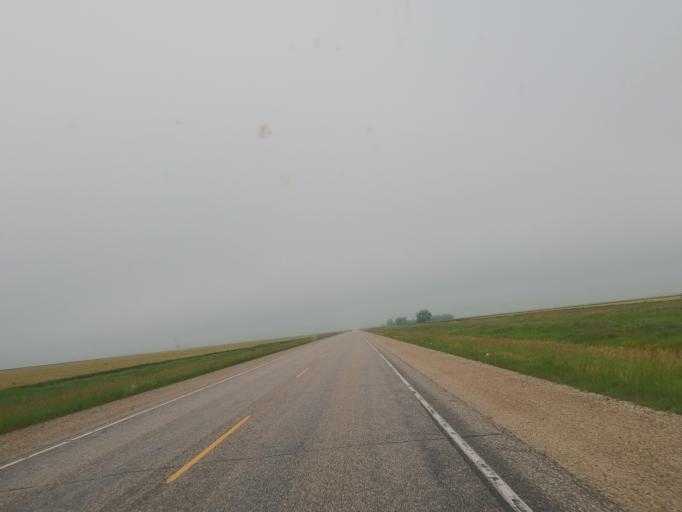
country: CA
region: Manitoba
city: Carman
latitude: 49.7293
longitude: -97.8633
